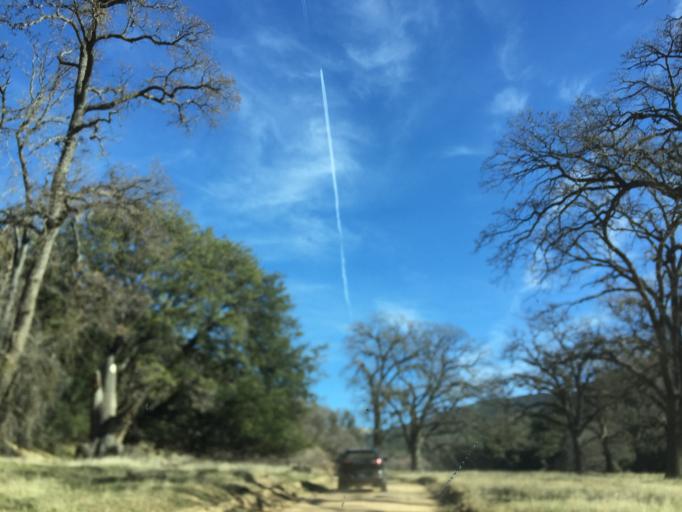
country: US
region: California
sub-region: Kern County
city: Lebec
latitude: 34.8976
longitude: -118.7326
